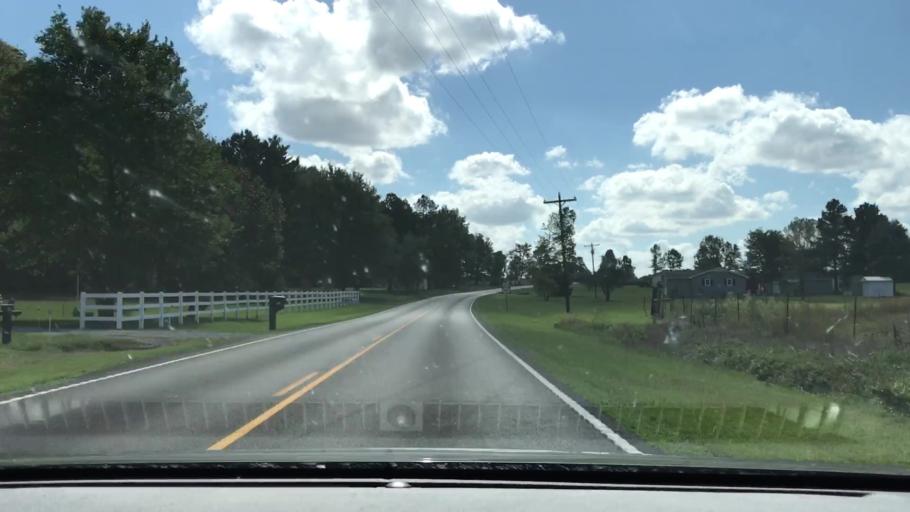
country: US
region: Kentucky
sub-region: Graves County
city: Mayfield
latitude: 36.8579
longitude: -88.5716
